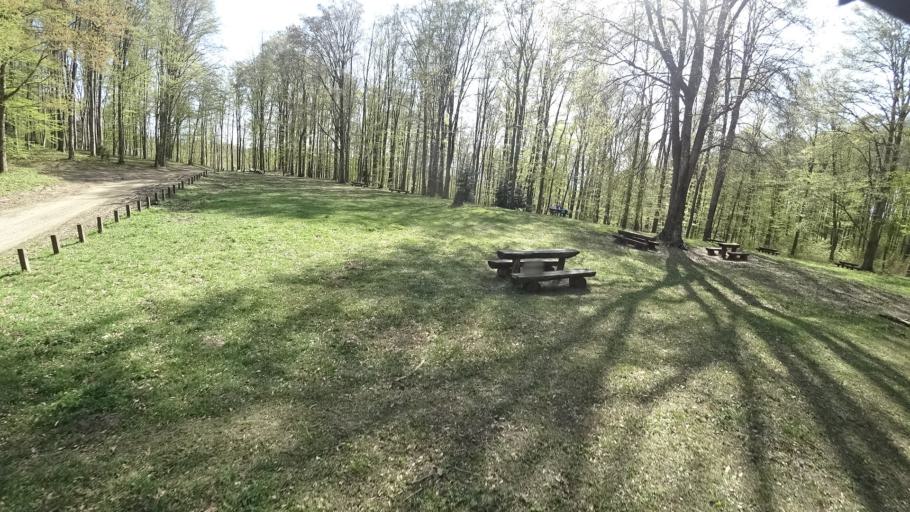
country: HR
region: Zagrebacka
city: Jablanovec
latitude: 45.8889
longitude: 15.9249
